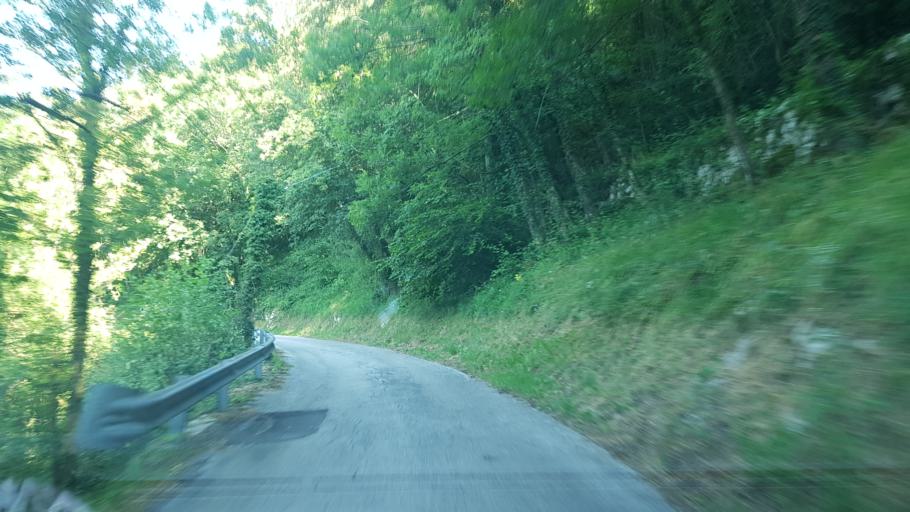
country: IT
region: Friuli Venezia Giulia
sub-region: Provincia di Udine
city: Nimis
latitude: 46.2322
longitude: 13.2464
